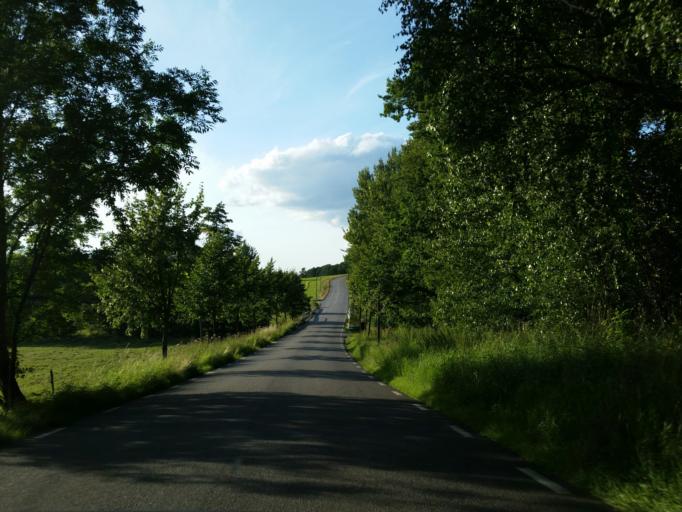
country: SE
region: Soedermanland
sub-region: Gnesta Kommun
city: Gnesta
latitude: 59.0178
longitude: 17.3646
